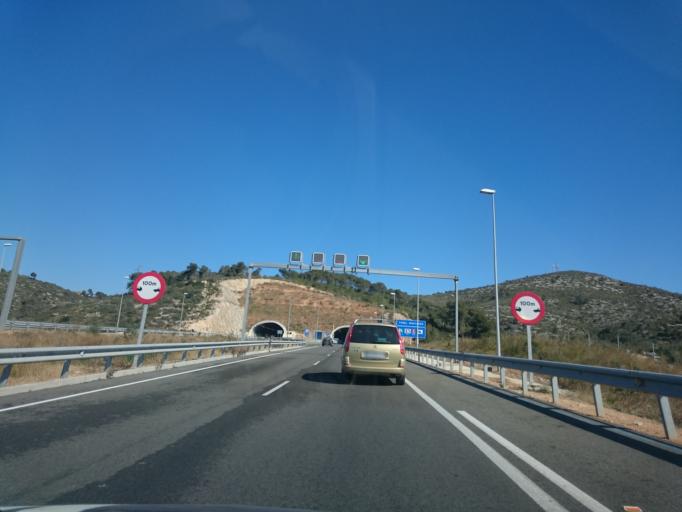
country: ES
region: Catalonia
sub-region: Provincia de Barcelona
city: Sant Pere de Ribes
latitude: 41.2587
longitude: 1.7324
